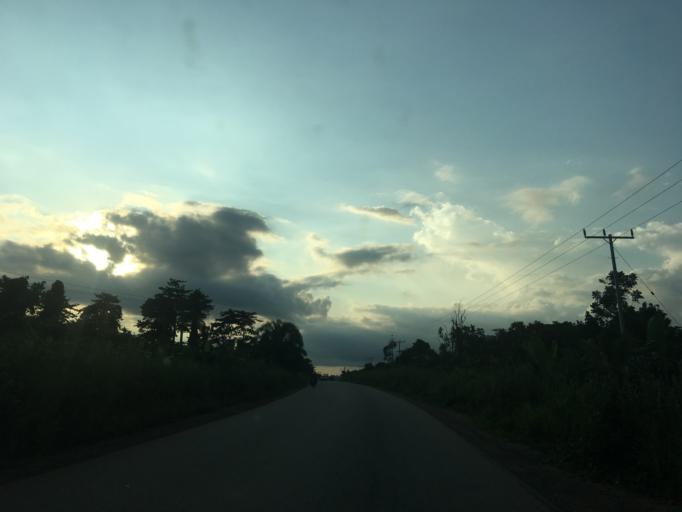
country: GH
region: Western
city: Bibiani
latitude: 6.6275
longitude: -2.4129
